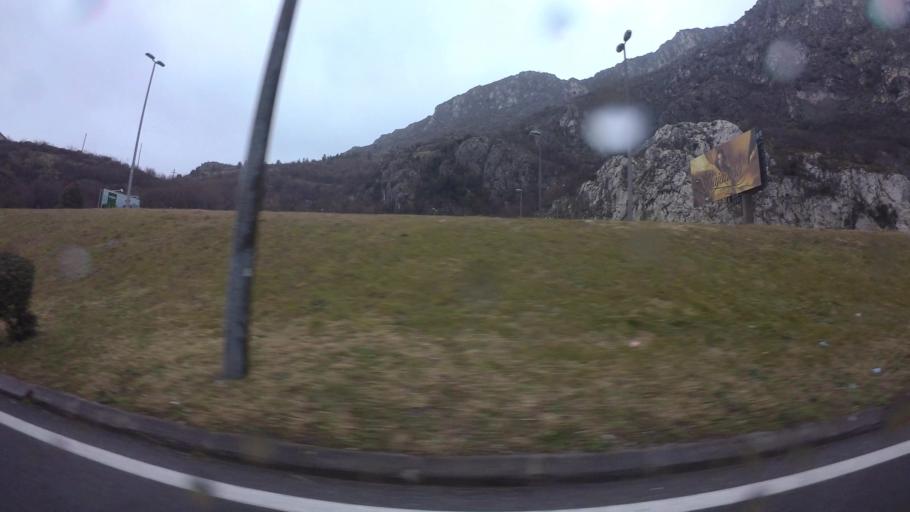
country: BA
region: Federation of Bosnia and Herzegovina
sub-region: Hercegovacko-Bosanski Kanton
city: Mostar
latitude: 43.3269
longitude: 17.8169
